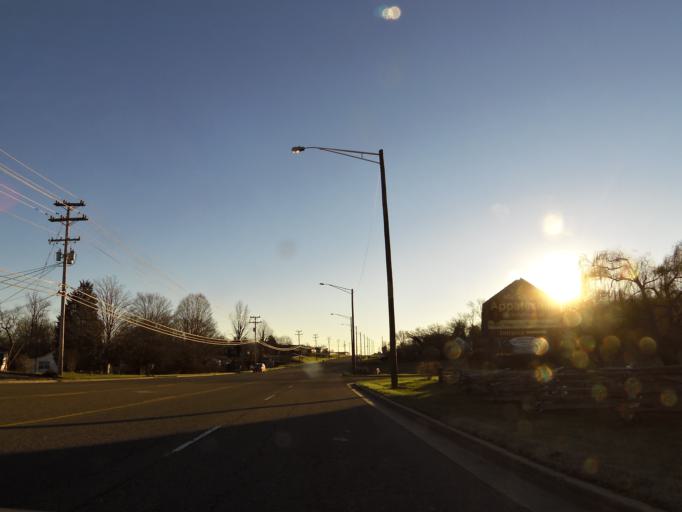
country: US
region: Tennessee
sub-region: Anderson County
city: Norris
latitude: 36.1776
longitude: -84.0694
